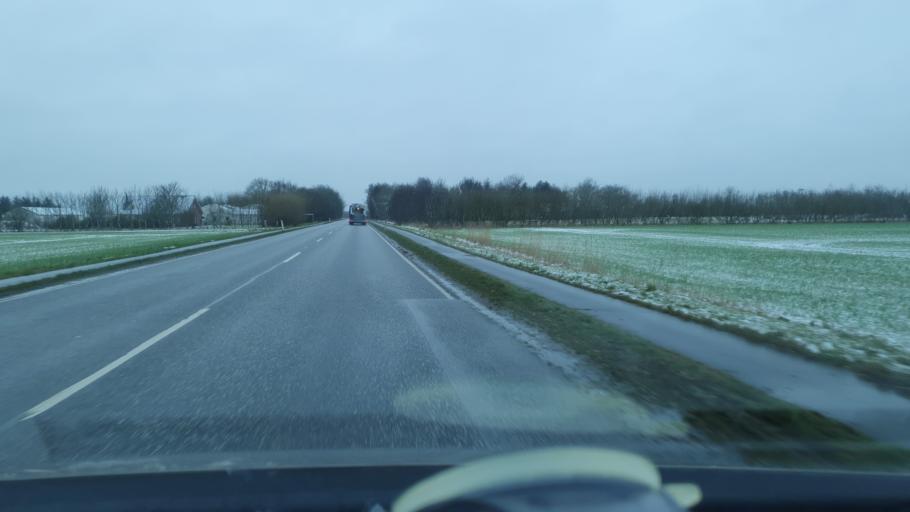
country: DK
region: North Denmark
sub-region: Jammerbugt Kommune
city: Brovst
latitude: 57.1182
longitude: 9.6118
